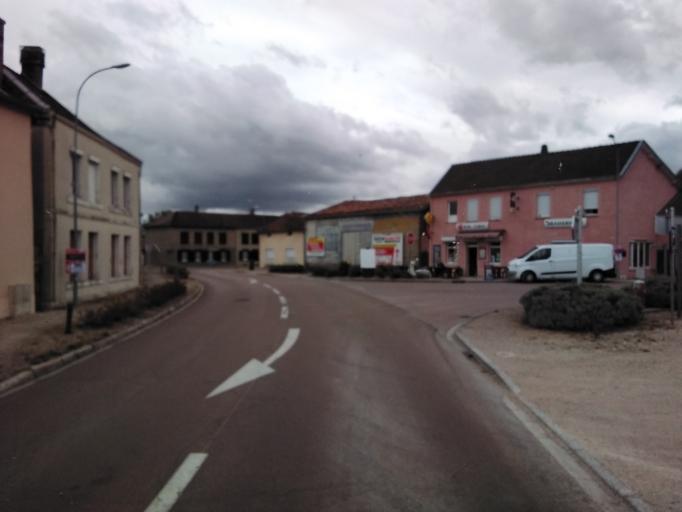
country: FR
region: Champagne-Ardenne
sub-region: Departement de l'Aube
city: Brienne-le-Chateau
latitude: 48.4618
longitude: 4.5015
